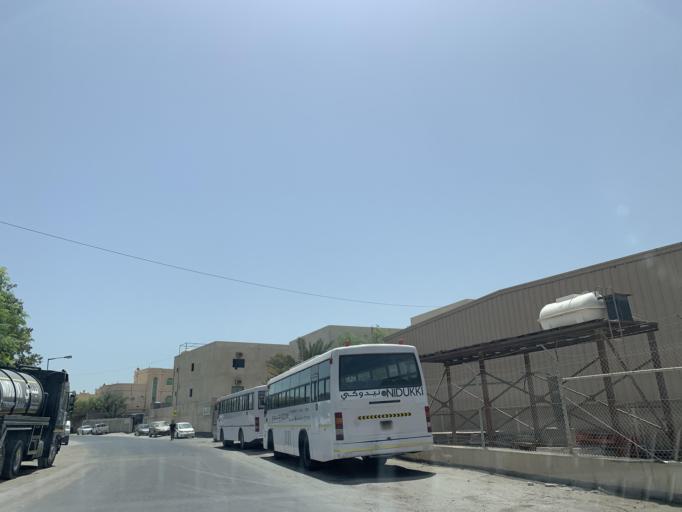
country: BH
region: Northern
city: Sitrah
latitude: 26.1729
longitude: 50.6050
